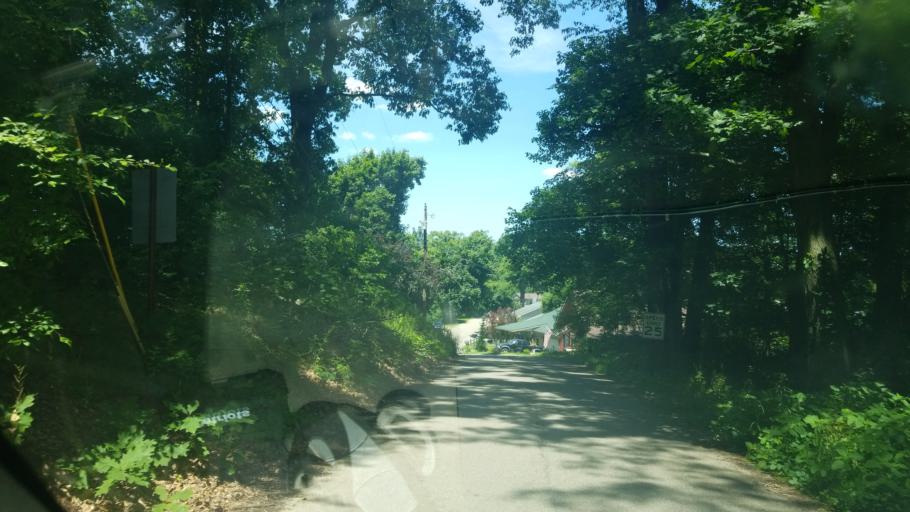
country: US
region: Ohio
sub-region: Mahoning County
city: Sebring
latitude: 40.8523
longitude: -80.9920
